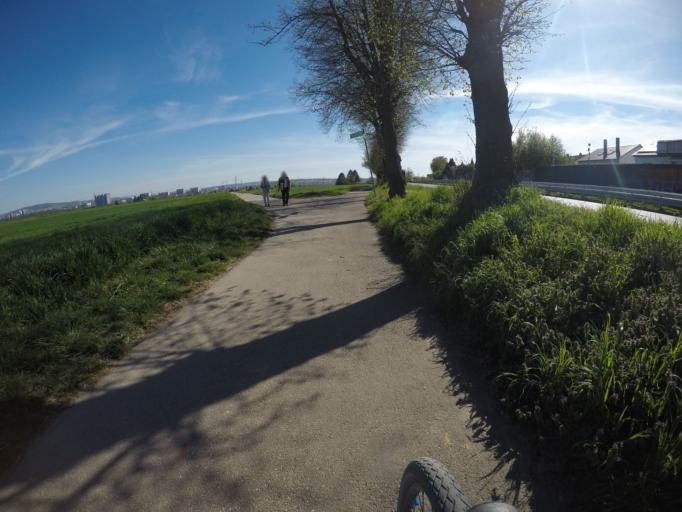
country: DE
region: Baden-Wuerttemberg
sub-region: Regierungsbezirk Stuttgart
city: Kornwestheim
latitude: 48.8565
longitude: 9.1960
